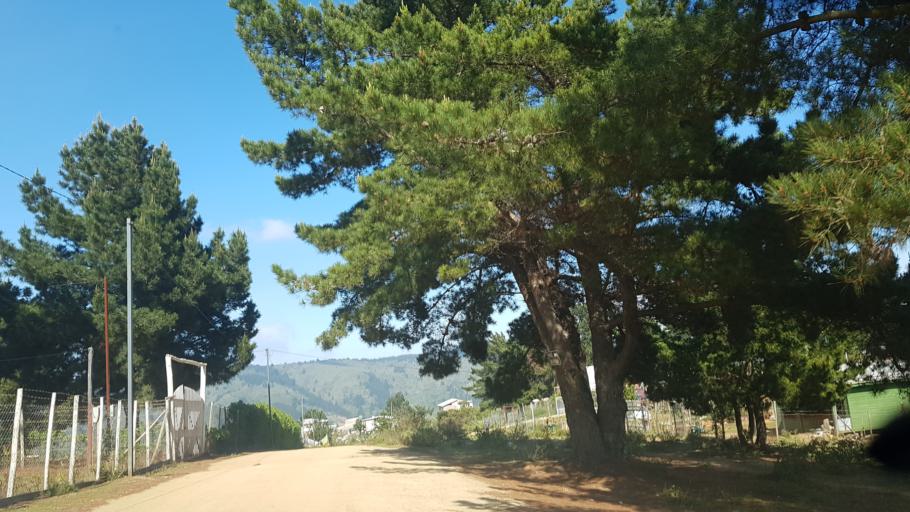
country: CL
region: Valparaiso
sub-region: Provincia de Valparaiso
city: Valparaiso
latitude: -33.1361
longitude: -71.6578
